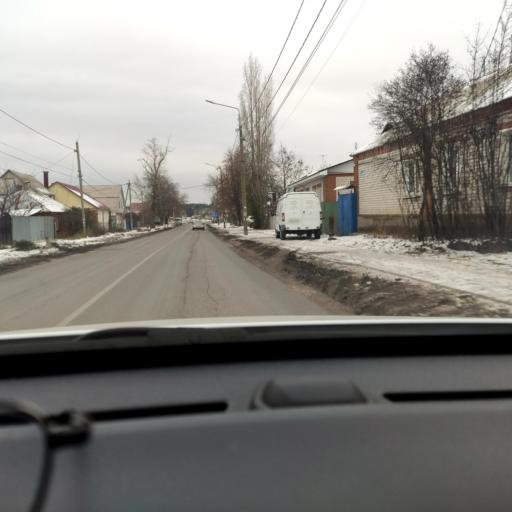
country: RU
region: Voronezj
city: Somovo
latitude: 51.7374
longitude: 39.2671
